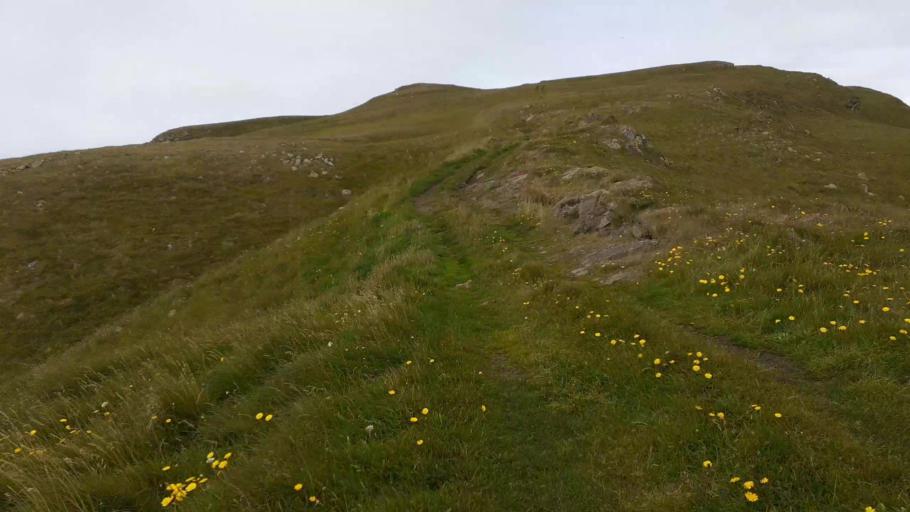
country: IS
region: Northeast
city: Dalvik
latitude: 66.5325
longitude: -17.9826
